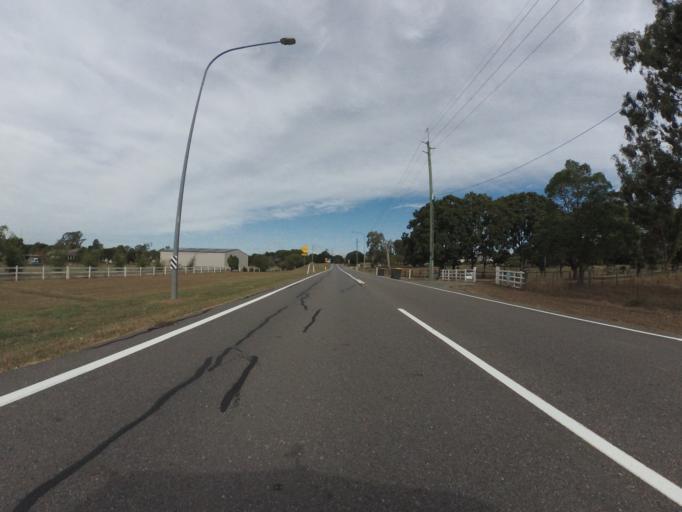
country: AU
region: Queensland
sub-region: Brisbane
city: Moggill
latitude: -27.5916
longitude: 152.8602
